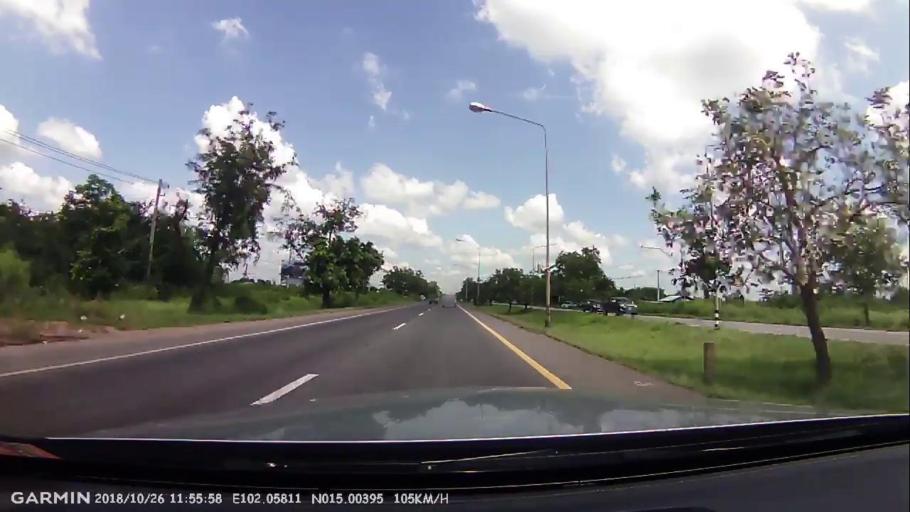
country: TH
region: Nakhon Ratchasima
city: Nakhon Ratchasima
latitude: 15.0040
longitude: 102.0582
